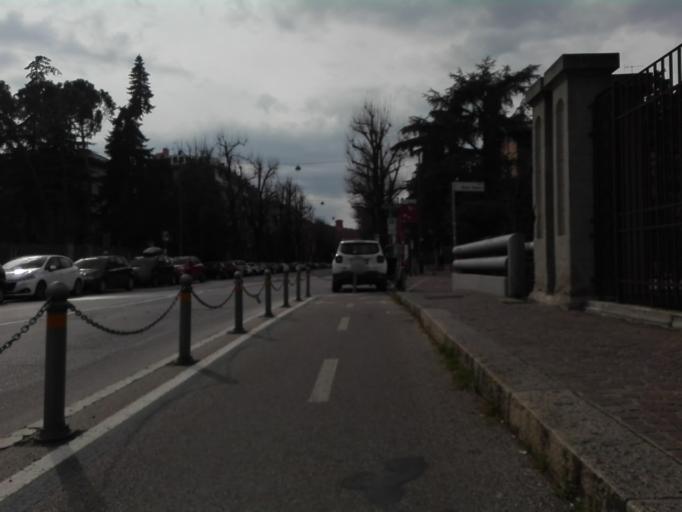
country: IT
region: Emilia-Romagna
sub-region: Provincia di Bologna
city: Bologna
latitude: 44.4874
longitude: 11.3573
